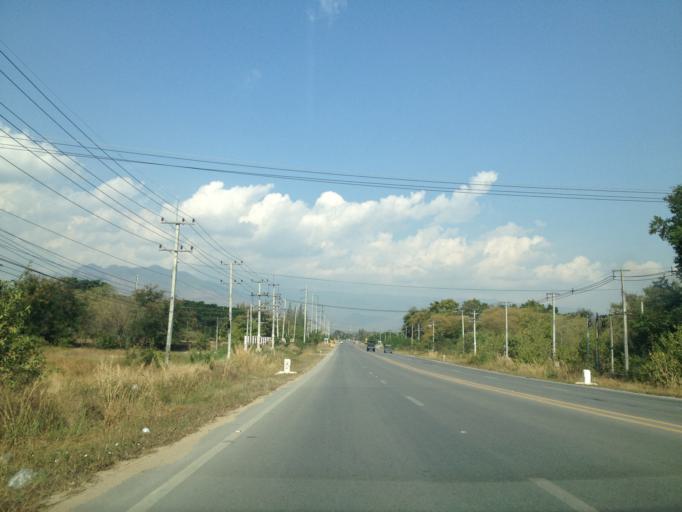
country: TH
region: Chiang Mai
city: Hot
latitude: 18.2215
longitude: 98.6143
